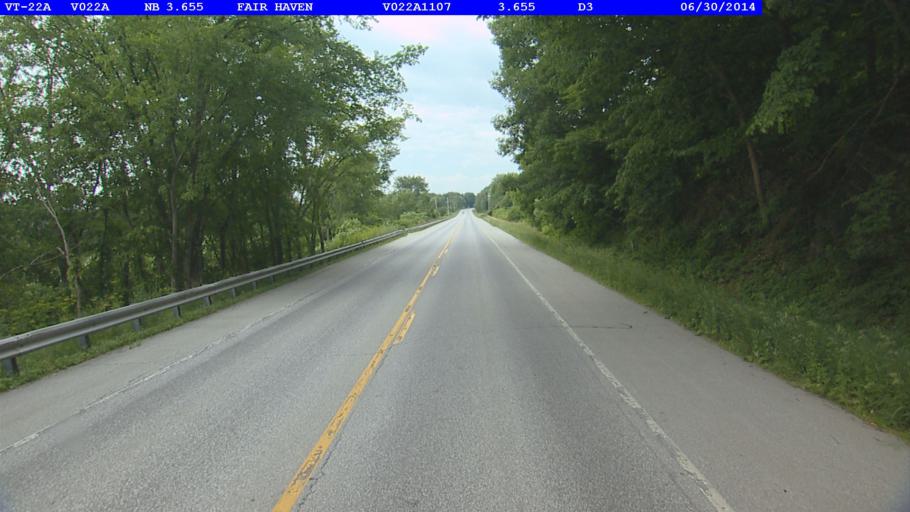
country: US
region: Vermont
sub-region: Rutland County
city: Fair Haven
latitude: 43.6172
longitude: -73.2950
